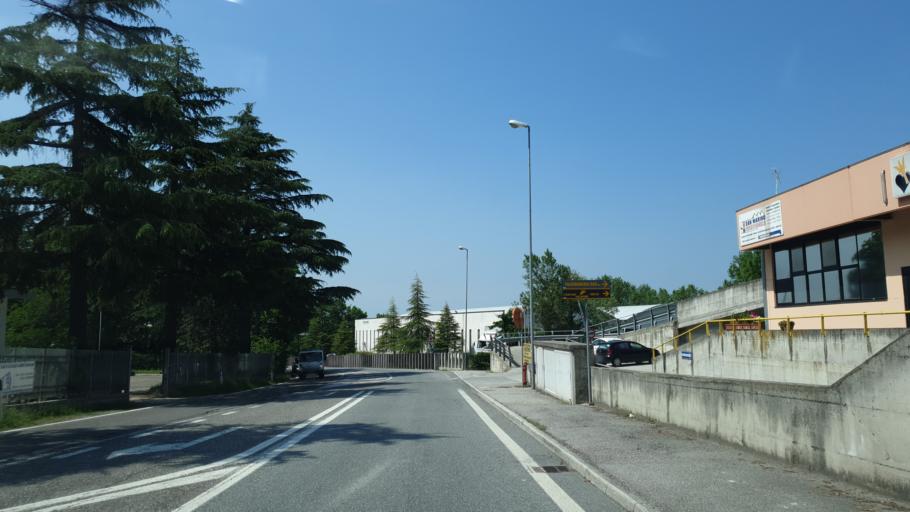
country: SM
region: Acquaviva
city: Acquaviva
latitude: 43.9437
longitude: 12.4311
